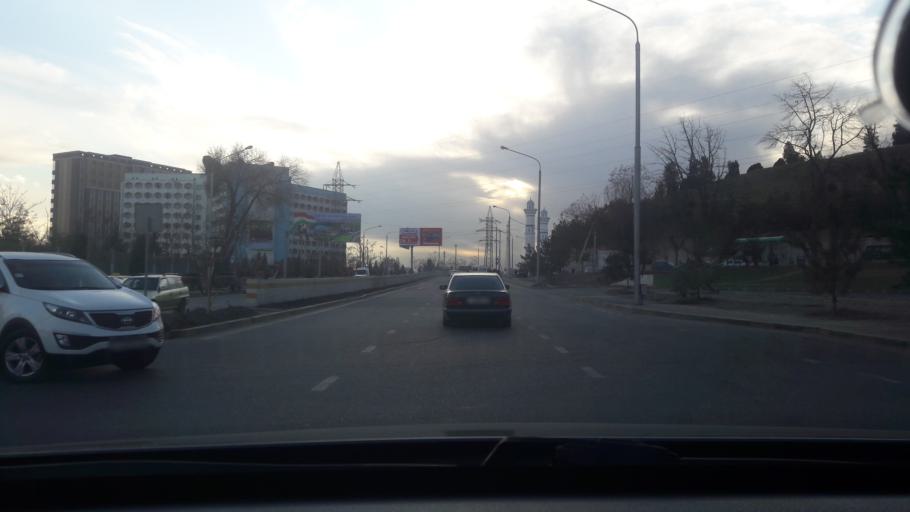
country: TJ
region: Dushanbe
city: Dushanbe
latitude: 38.5993
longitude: 68.7700
